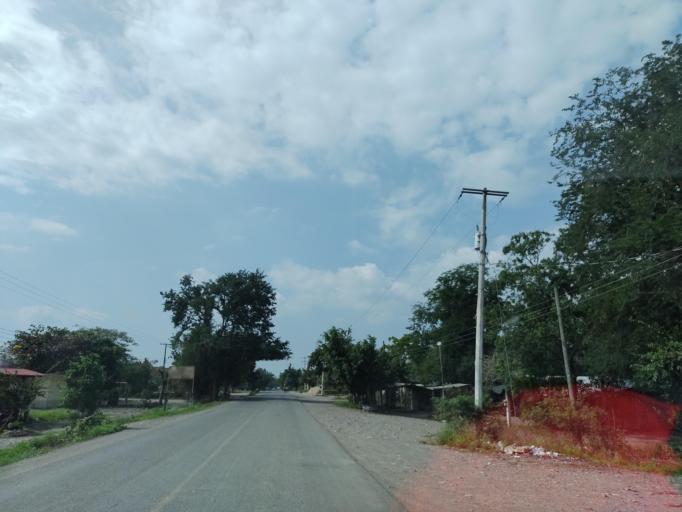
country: MX
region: Puebla
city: Espinal
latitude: 20.2732
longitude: -97.3329
